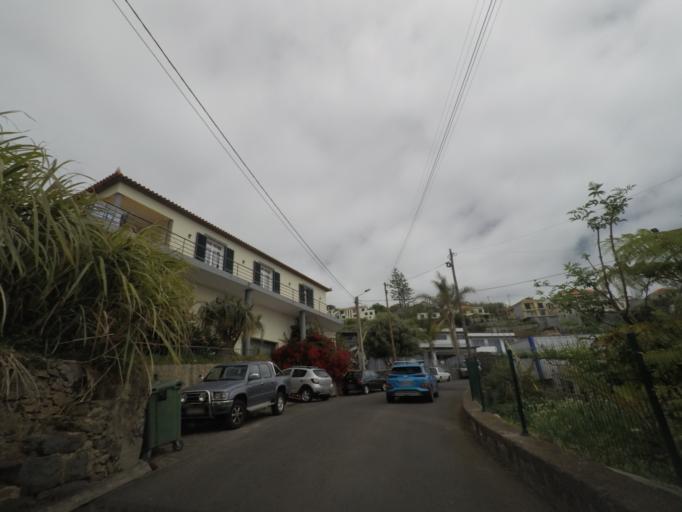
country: PT
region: Madeira
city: Ponta do Sol
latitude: 32.6920
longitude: -17.0986
